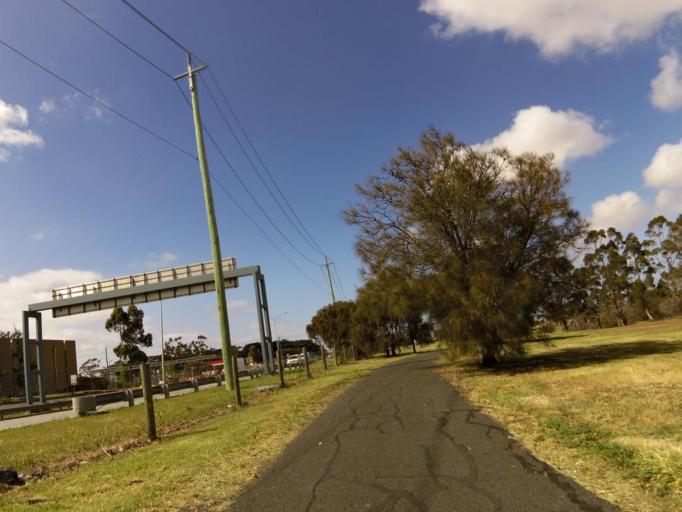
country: AU
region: Victoria
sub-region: Brimbank
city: Keilor Park
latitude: -37.7280
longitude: 144.8494
